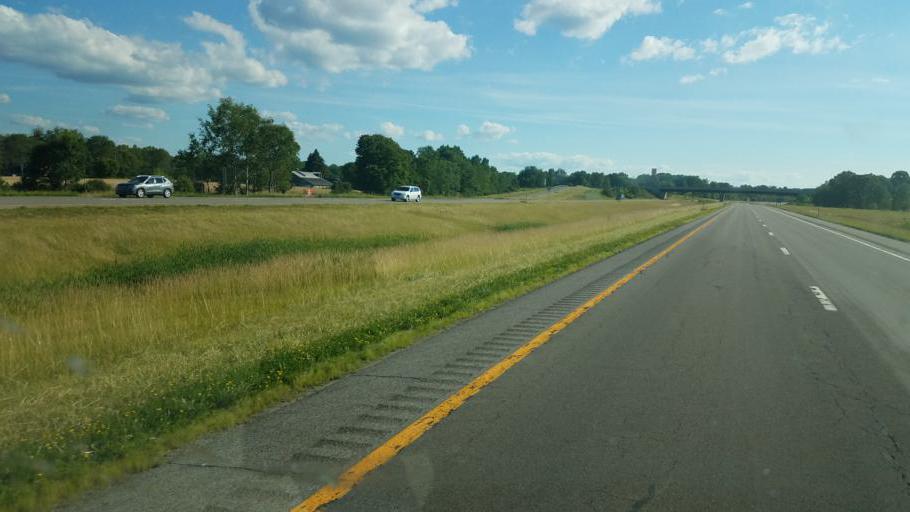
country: US
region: New York
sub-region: Chautauqua County
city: Falconer
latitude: 42.1322
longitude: -79.1868
